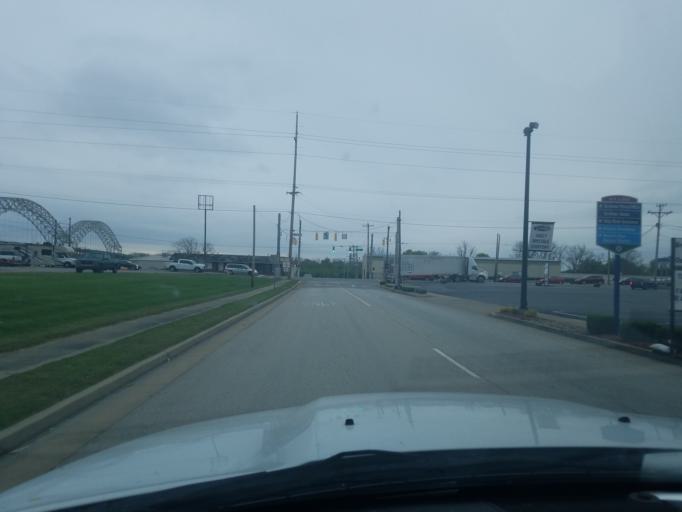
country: US
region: Indiana
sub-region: Floyd County
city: New Albany
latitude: 38.2819
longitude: -85.8288
